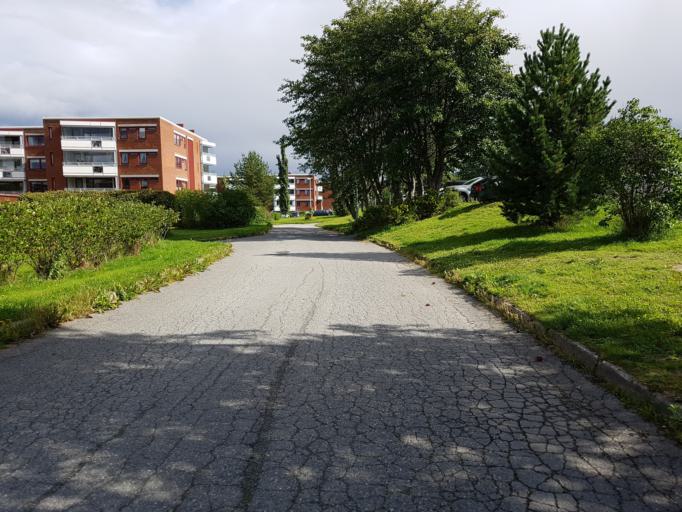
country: NO
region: Sor-Trondelag
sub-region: Trondheim
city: Trondheim
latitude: 63.4158
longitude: 10.4810
